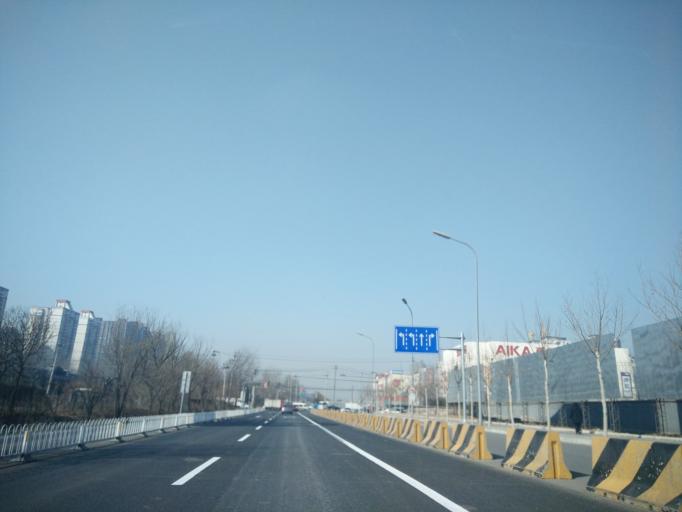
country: CN
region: Beijing
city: Wangjing
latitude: 40.0146
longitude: 116.4629
